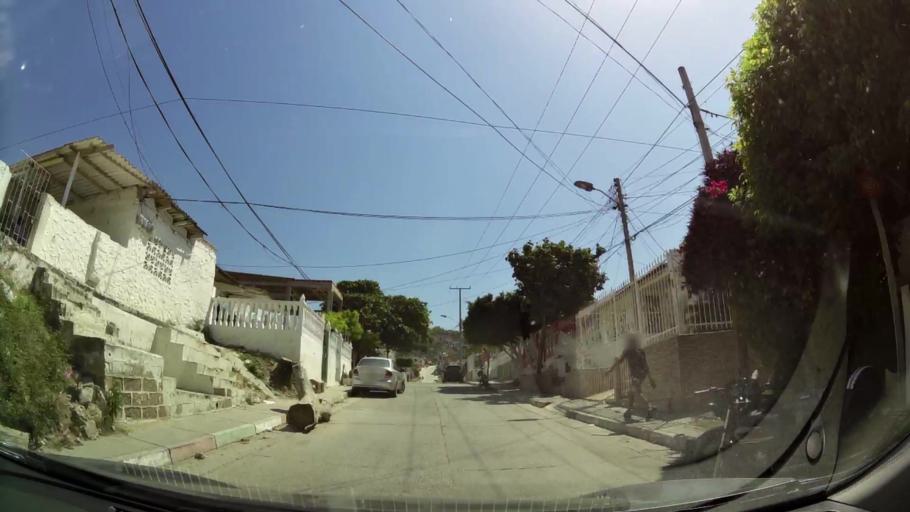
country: CO
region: Bolivar
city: Cartagena
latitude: 10.4320
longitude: -75.5298
